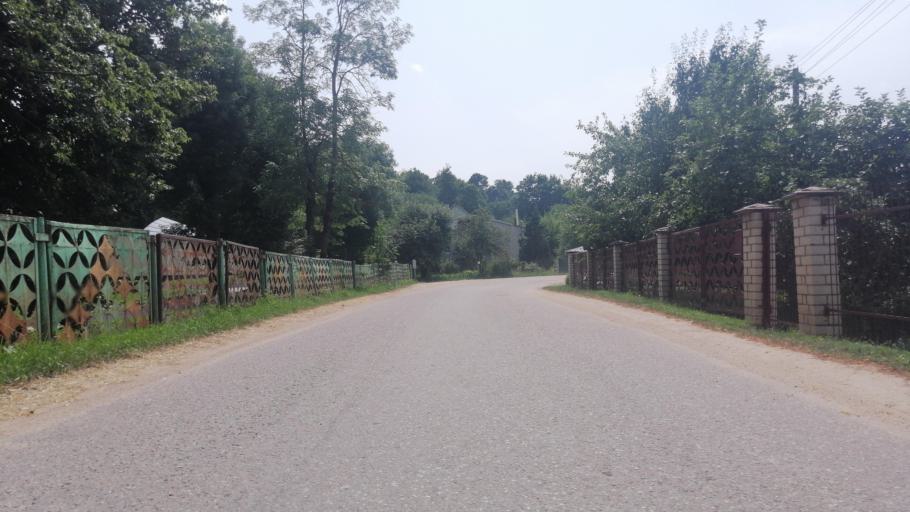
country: BY
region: Grodnenskaya
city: Navahrudak
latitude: 53.6049
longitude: 25.8263
